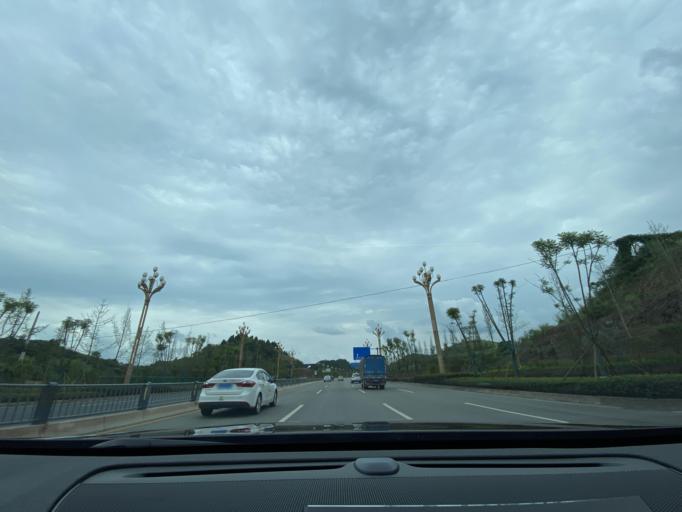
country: CN
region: Sichuan
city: Jiancheng
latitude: 30.4734
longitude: 104.4912
